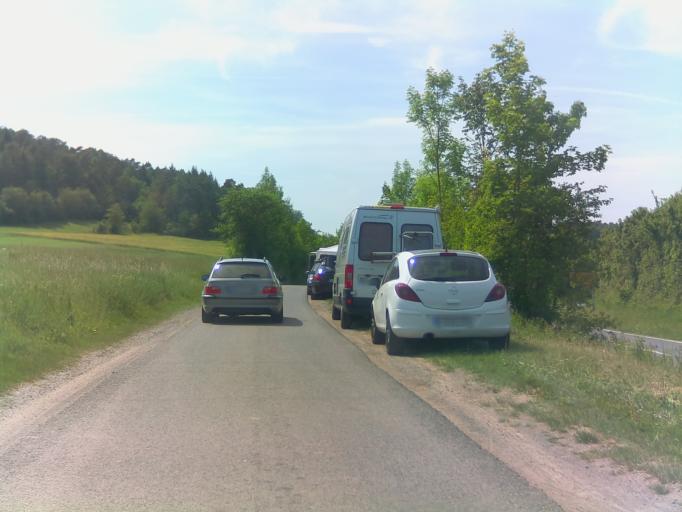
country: DE
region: Bavaria
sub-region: Regierungsbezirk Unterfranken
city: Karbach
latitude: 49.8636
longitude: 9.6387
